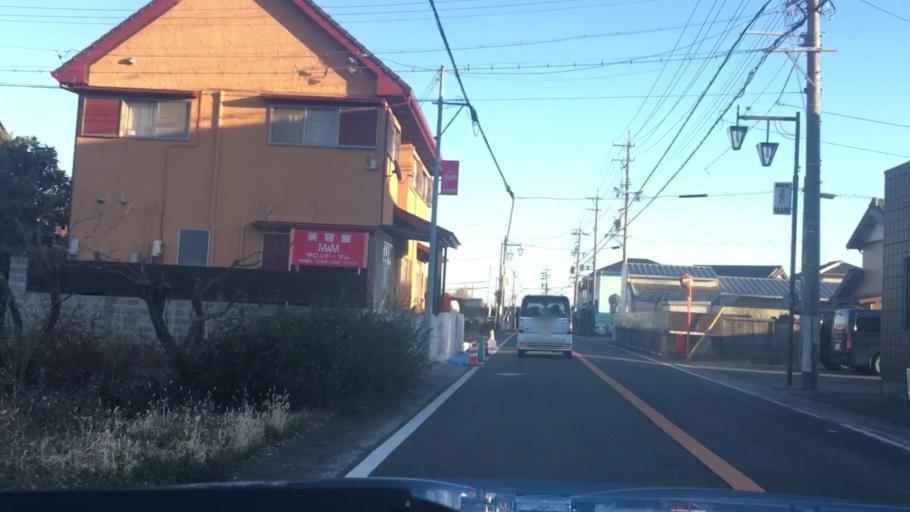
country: JP
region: Shizuoka
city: Hamamatsu
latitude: 34.7384
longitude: 137.6828
